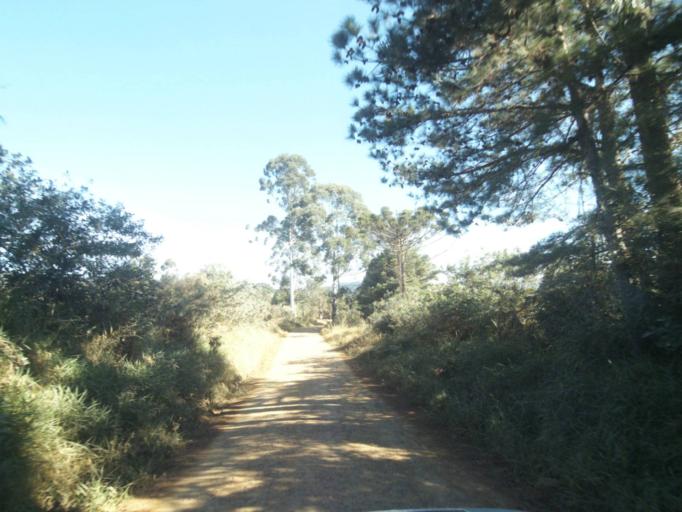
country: BR
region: Parana
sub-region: Tibagi
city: Tibagi
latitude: -24.5435
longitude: -50.5076
